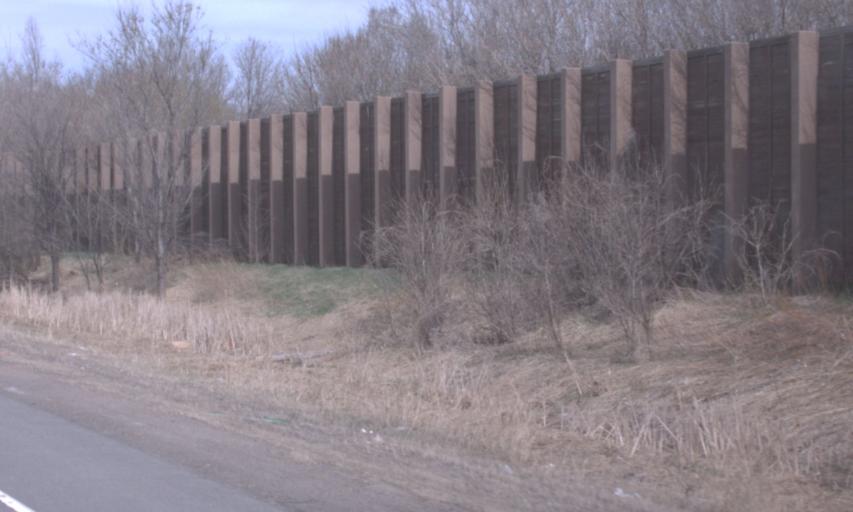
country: US
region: Minnesota
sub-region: Anoka County
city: Coon Rapids
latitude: 45.1583
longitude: -93.2803
